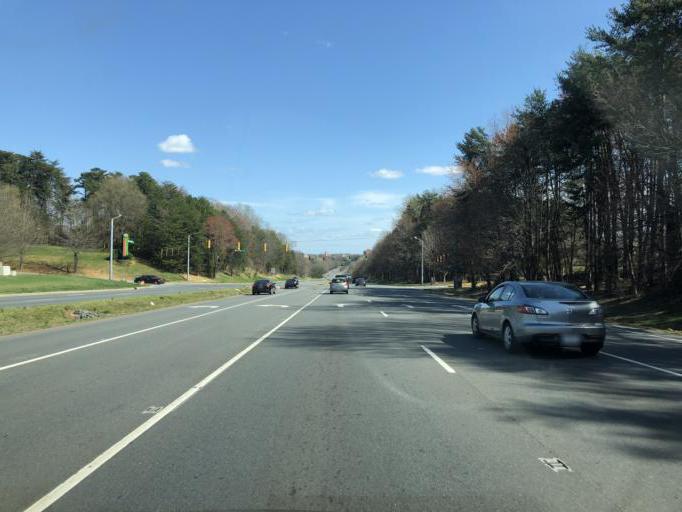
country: US
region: North Carolina
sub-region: Mecklenburg County
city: Charlotte
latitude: 35.3165
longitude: -80.7727
